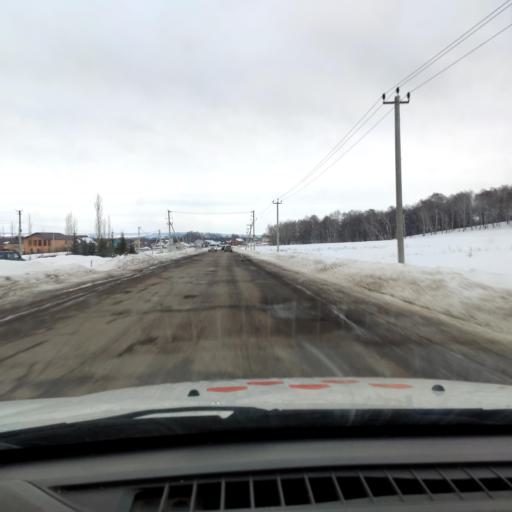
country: RU
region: Bashkortostan
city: Avdon
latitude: 54.6218
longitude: 55.6759
